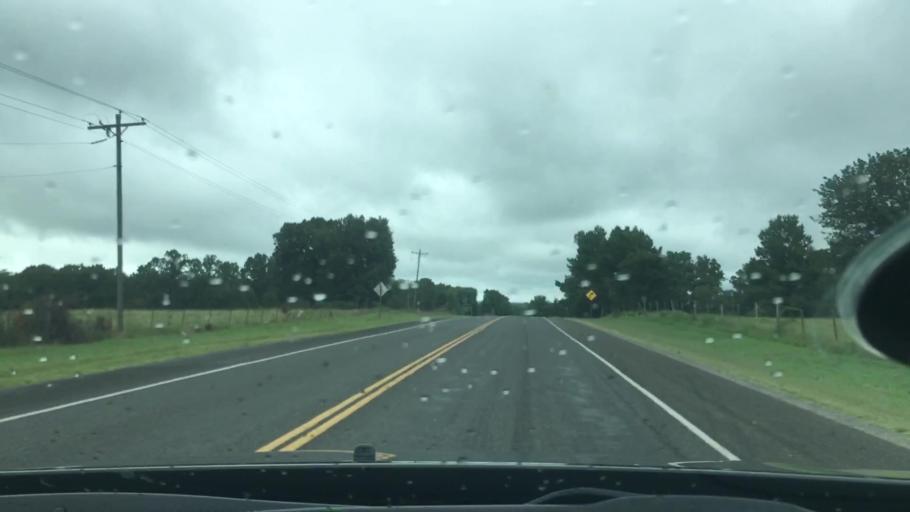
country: US
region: Oklahoma
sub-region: Sequoyah County
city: Vian
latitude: 35.5714
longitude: -94.9852
